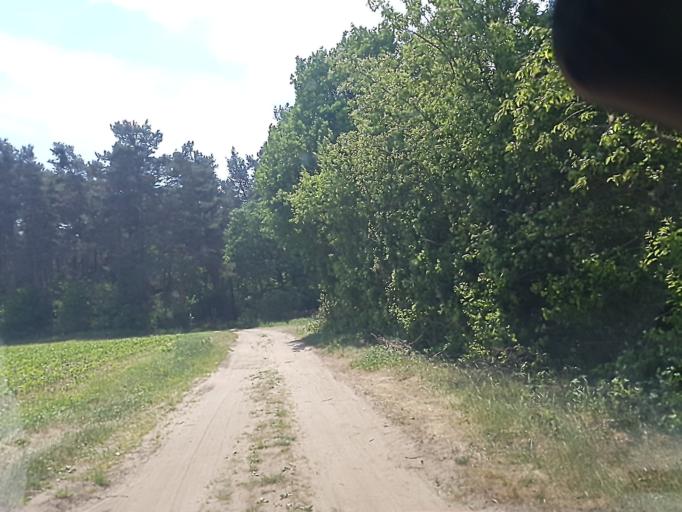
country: DE
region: Brandenburg
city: Gorzke
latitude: 52.1257
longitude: 12.3126
